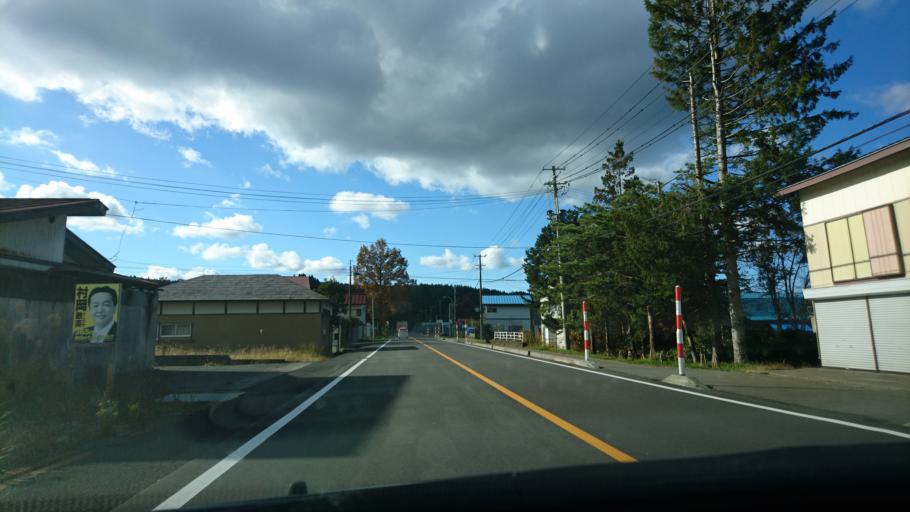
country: JP
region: Akita
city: Omagari
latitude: 39.3073
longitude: 140.2778
